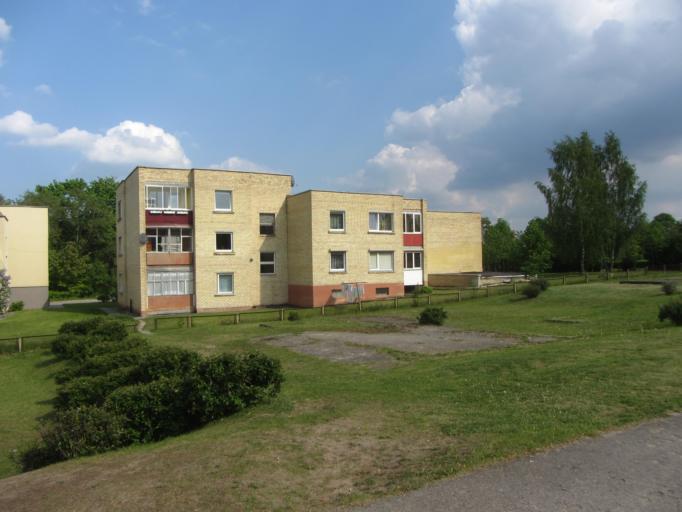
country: LT
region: Utenos apskritis
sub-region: Utena
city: Utena
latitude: 55.5108
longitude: 25.5913
